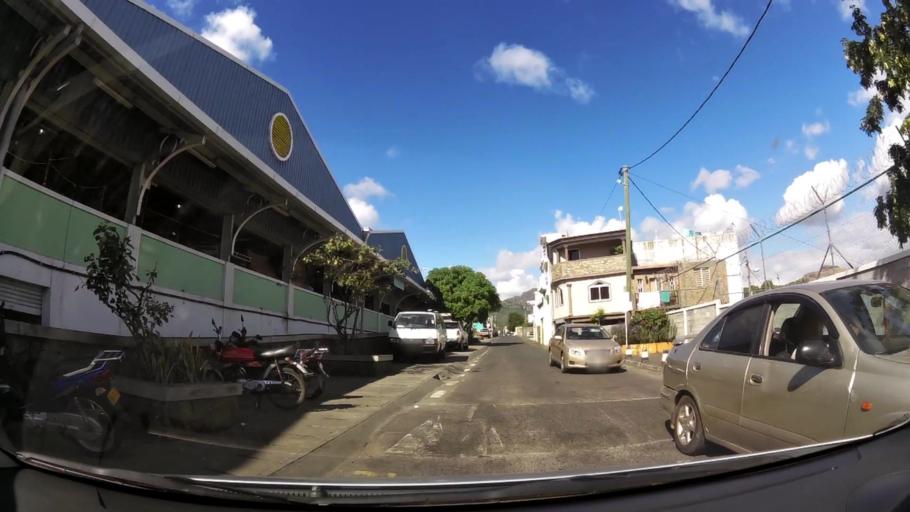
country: MU
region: Pamplemousses
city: Le Hochet
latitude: -20.1558
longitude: 57.5196
